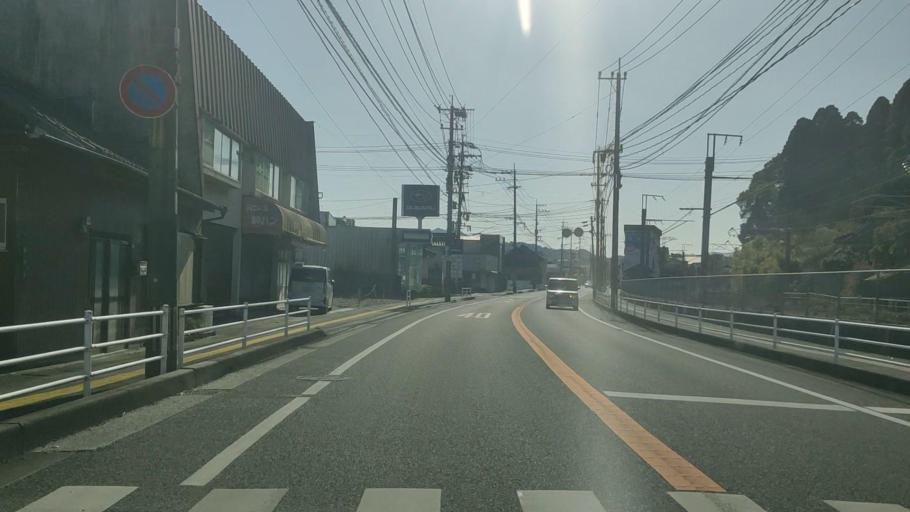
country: JP
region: Oita
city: Saiki
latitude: 32.9692
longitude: 131.9028
